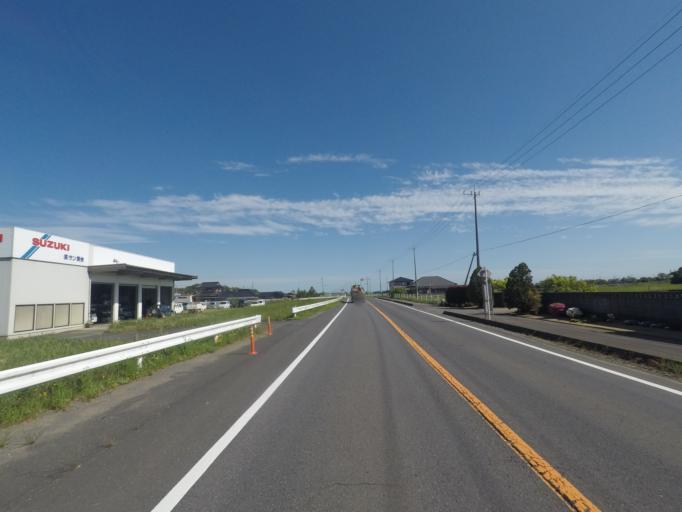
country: JP
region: Ibaraki
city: Inashiki
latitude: 36.0714
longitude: 140.4239
